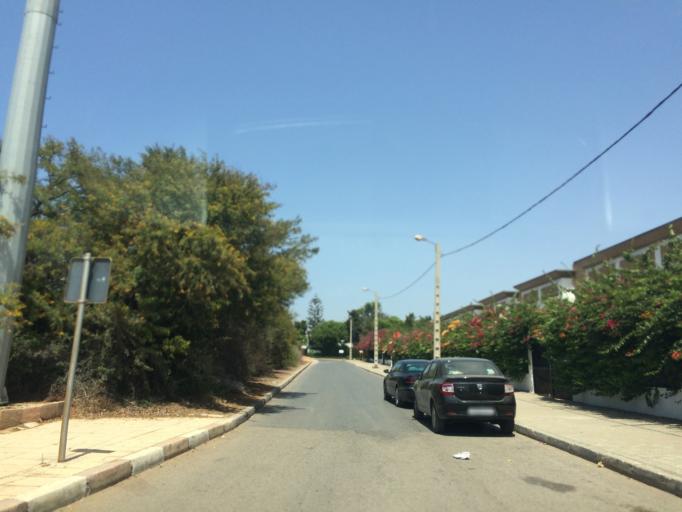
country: MA
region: Rabat-Sale-Zemmour-Zaer
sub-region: Skhirate-Temara
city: Temara
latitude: 33.9311
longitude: -6.9292
